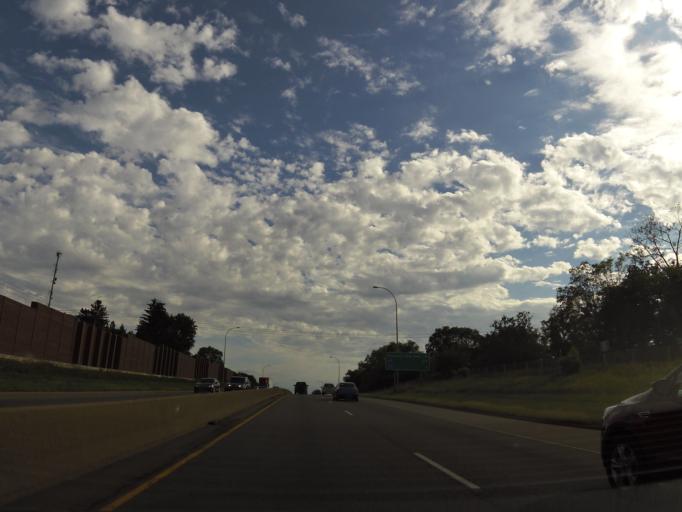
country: US
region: Minnesota
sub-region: Hennepin County
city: New Hope
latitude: 45.0029
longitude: -93.4010
